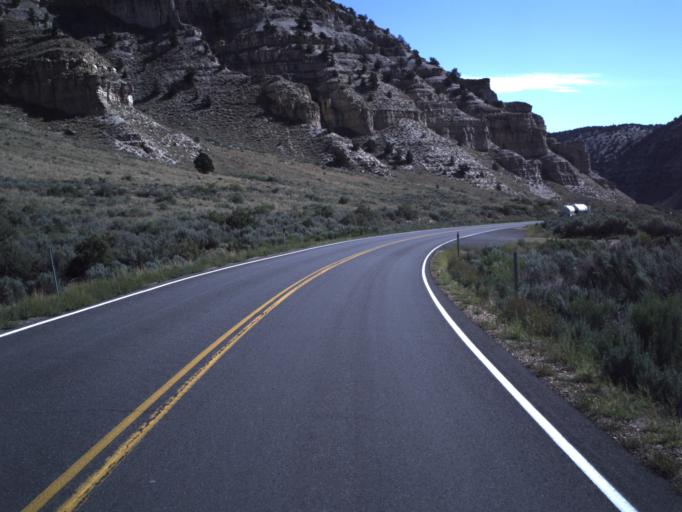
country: US
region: Utah
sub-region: Duchesne County
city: Duchesne
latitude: 40.0453
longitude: -110.5362
